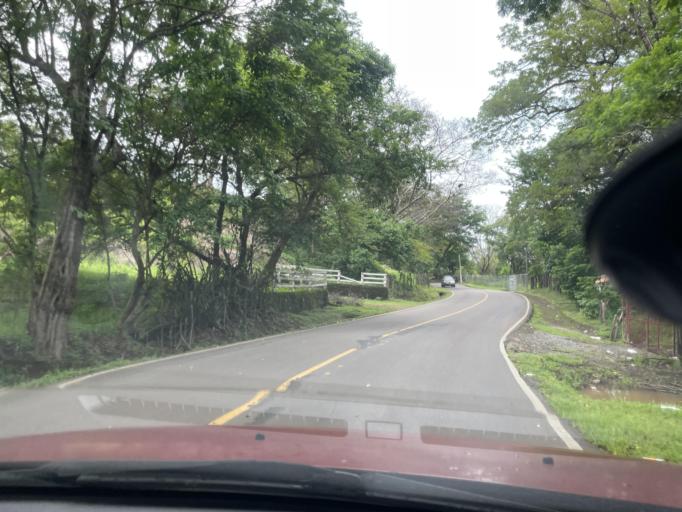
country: SV
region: La Union
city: Santa Rosa de Lima
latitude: 13.6460
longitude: -87.8563
